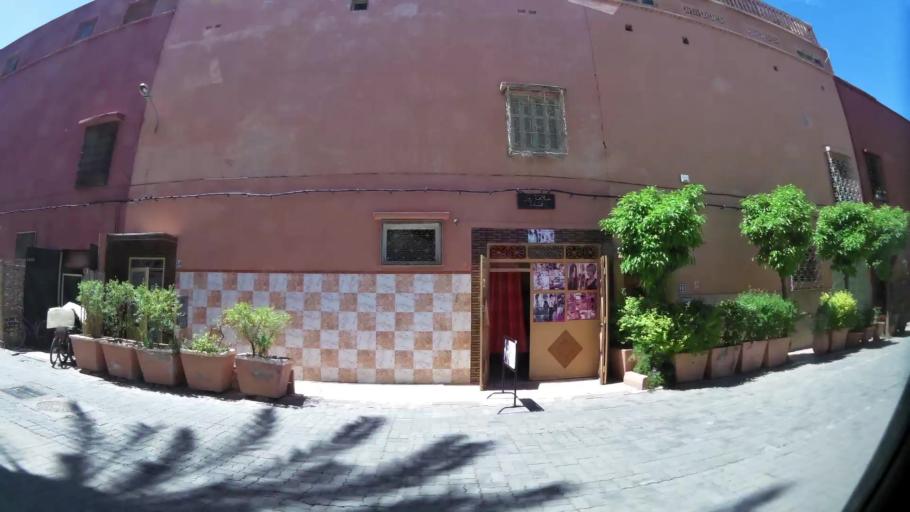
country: MA
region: Marrakech-Tensift-Al Haouz
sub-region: Marrakech
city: Marrakesh
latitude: 31.6472
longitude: -7.9938
